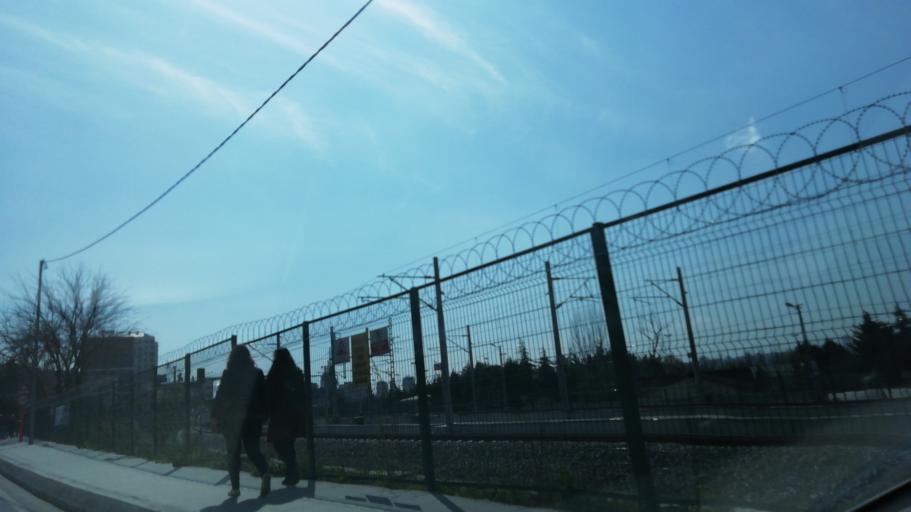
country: TR
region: Istanbul
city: Mahmutbey
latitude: 41.0077
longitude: 28.7751
